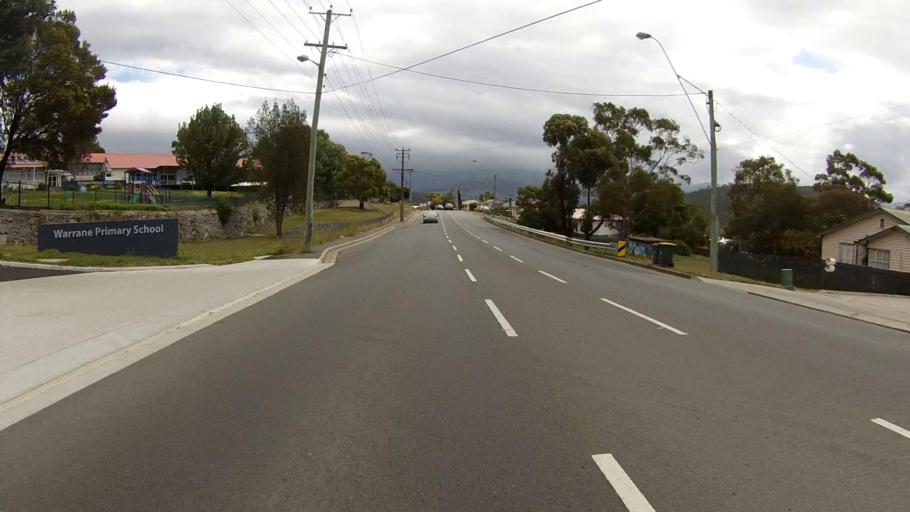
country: AU
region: Tasmania
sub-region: Clarence
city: Warrane
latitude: -42.8599
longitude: 147.3825
